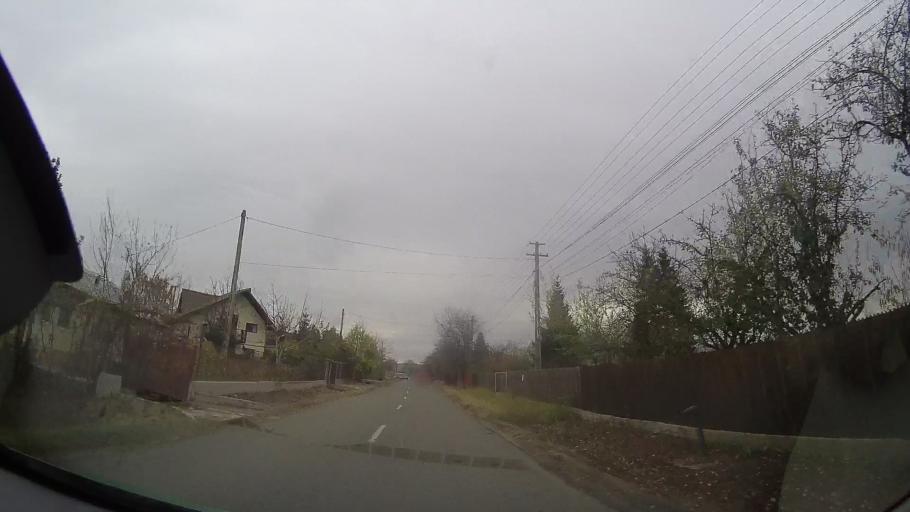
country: RO
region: Prahova
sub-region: Comuna Fantanele
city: Fantanele
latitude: 45.0135
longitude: 26.3794
